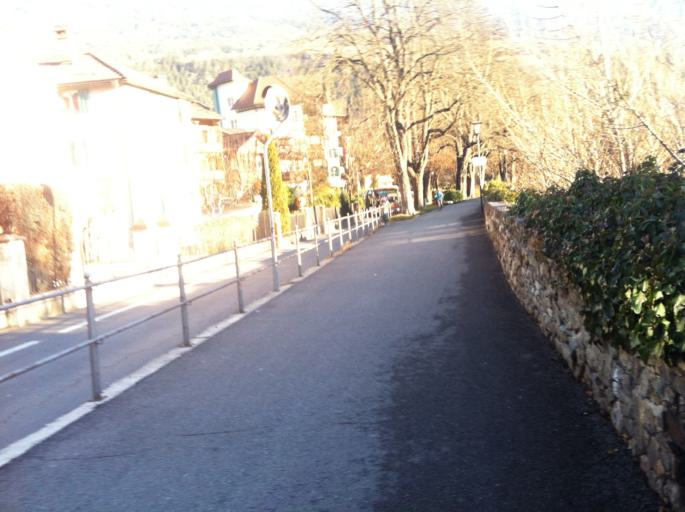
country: IT
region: Trentino-Alto Adige
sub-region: Bolzano
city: Bressanone
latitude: 46.7164
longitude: 11.6598
